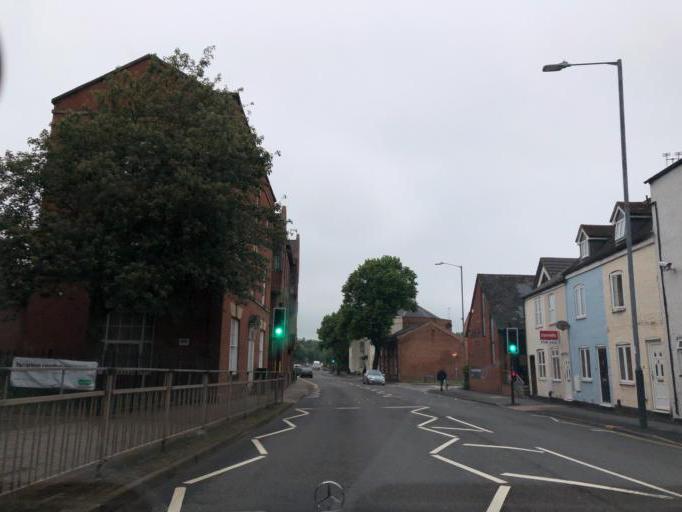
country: GB
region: England
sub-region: Warwickshire
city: Warwick
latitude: 52.2846
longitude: -1.5924
